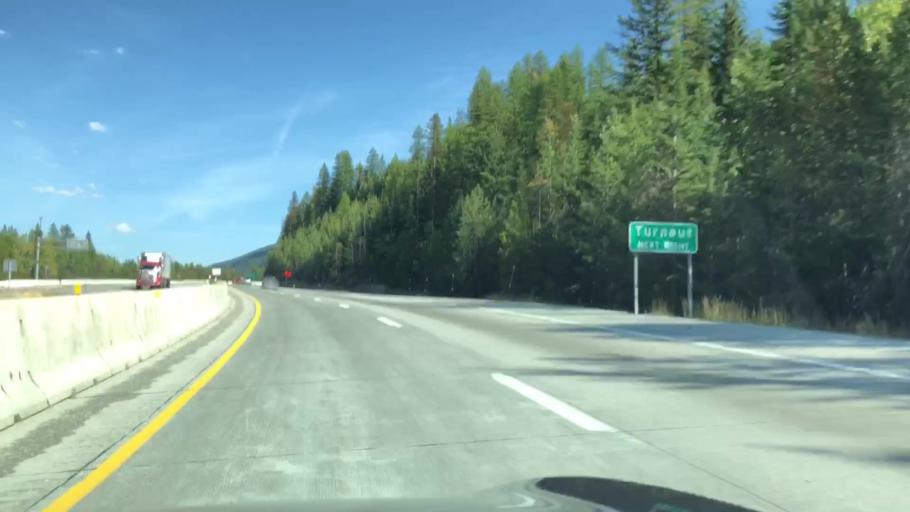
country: US
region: Idaho
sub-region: Shoshone County
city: Wallace
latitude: 47.4650
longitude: -115.7552
